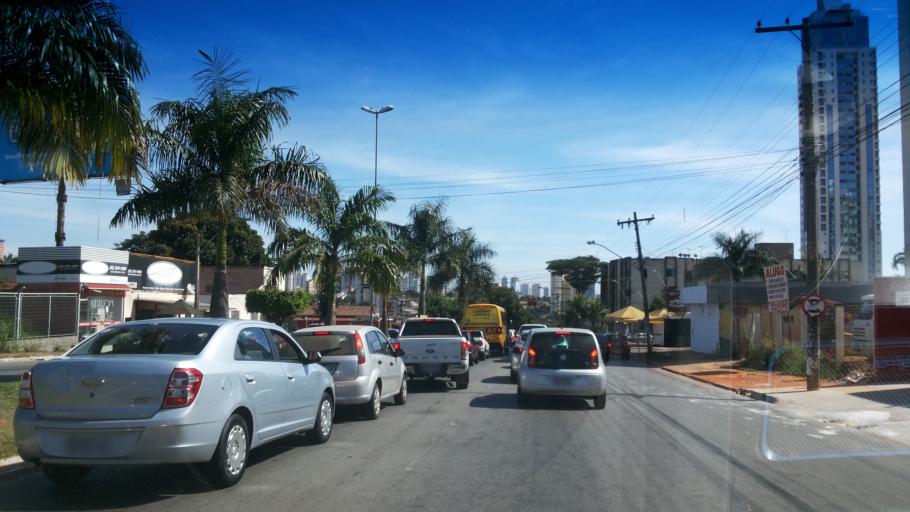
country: BR
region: Goias
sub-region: Goiania
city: Goiania
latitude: -16.7162
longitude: -49.2400
